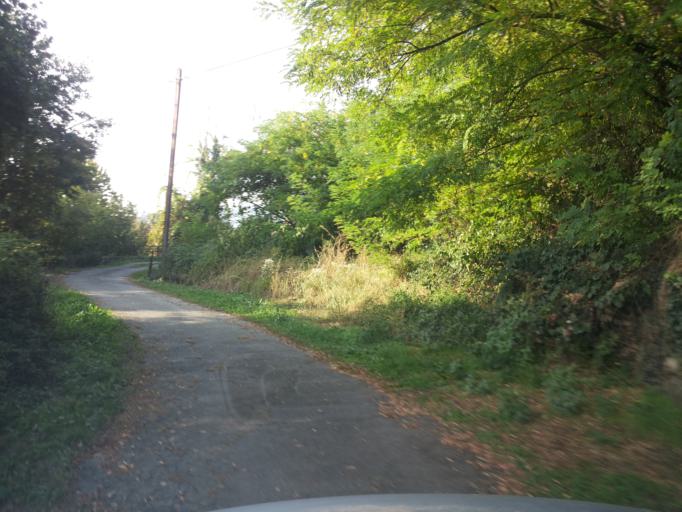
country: IT
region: Piedmont
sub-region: Provincia di Biella
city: Viverone
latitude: 45.4324
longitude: 8.0461
